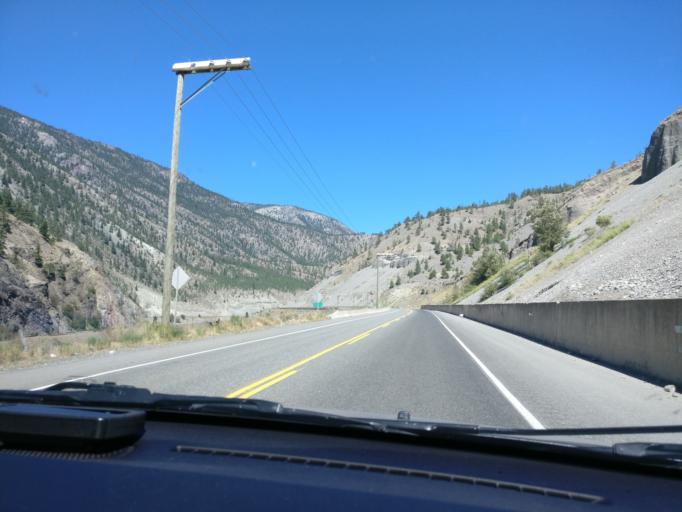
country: CA
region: British Columbia
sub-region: Thompson-Nicola Regional District
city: Ashcroft
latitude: 50.2708
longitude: -121.4014
